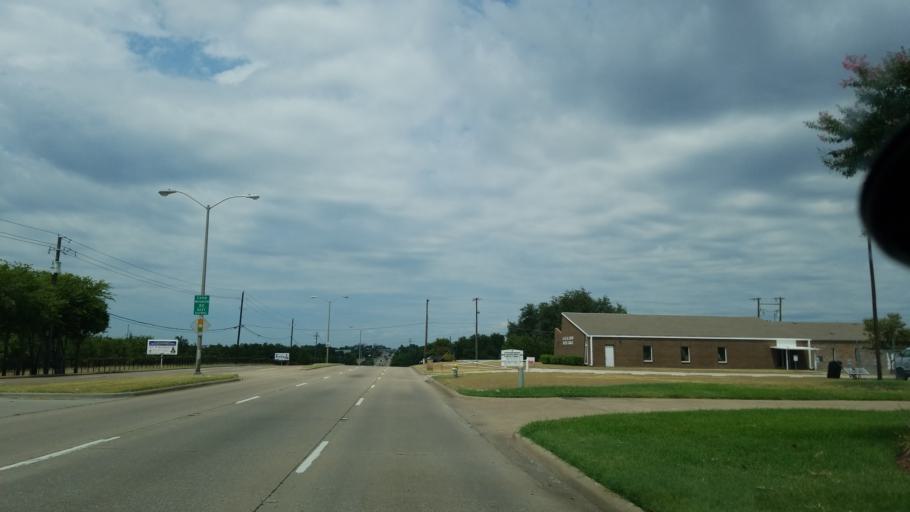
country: US
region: Texas
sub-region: Dallas County
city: Duncanville
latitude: 32.6594
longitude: -96.8573
